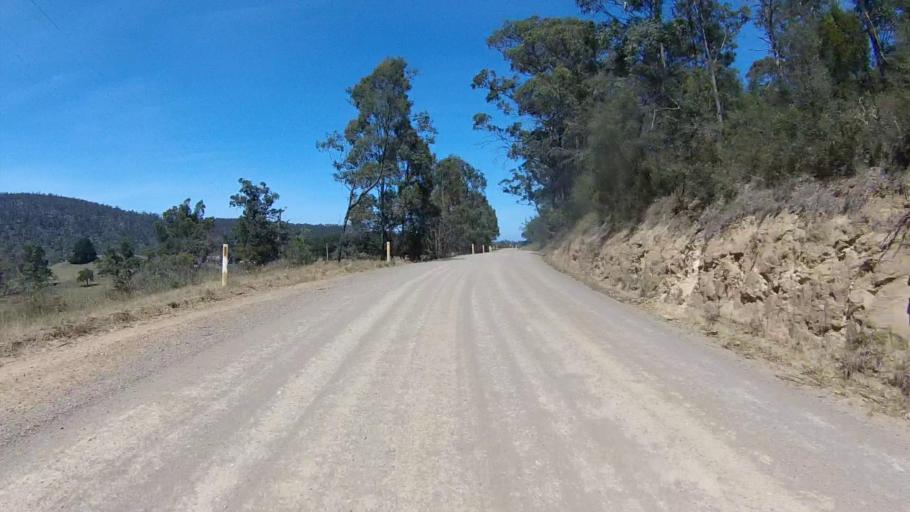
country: AU
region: Tasmania
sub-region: Sorell
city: Sorell
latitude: -42.7563
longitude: 147.6827
